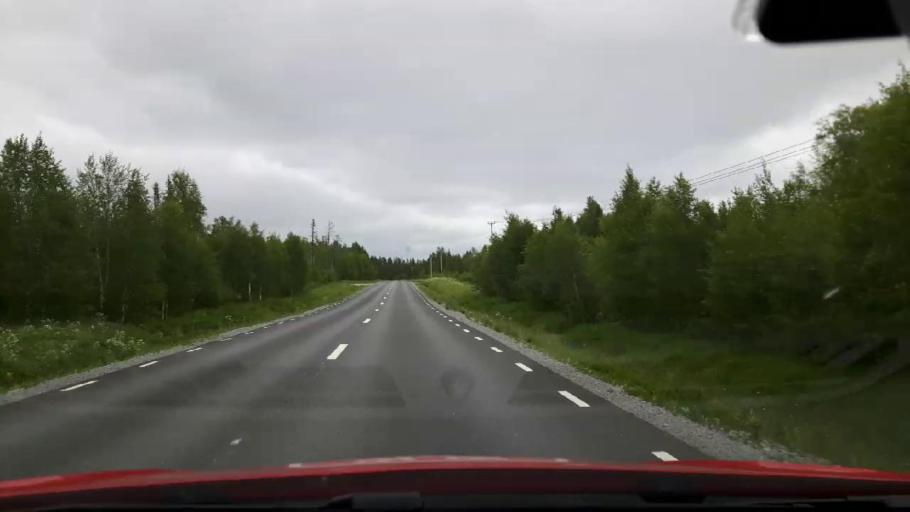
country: SE
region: Jaemtland
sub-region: OEstersunds Kommun
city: Lit
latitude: 63.7381
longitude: 14.7671
